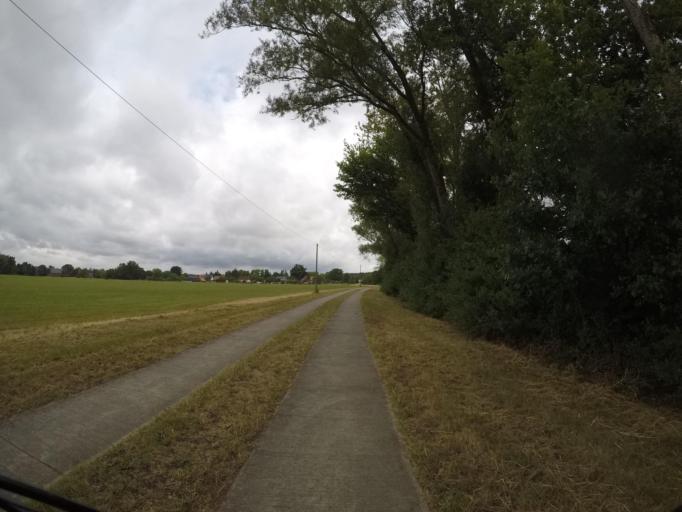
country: DE
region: Lower Saxony
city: Hitzacker
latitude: 53.1785
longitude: 11.1103
